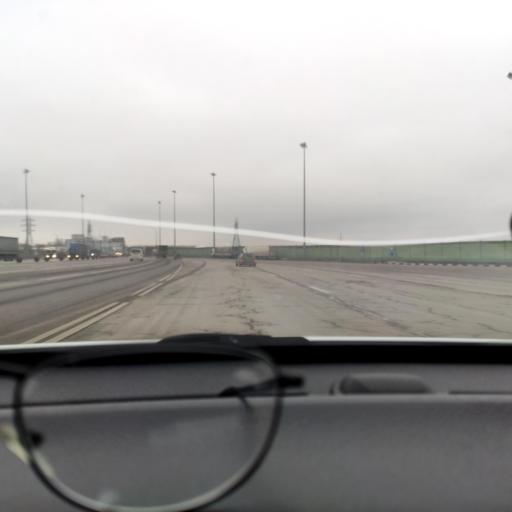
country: RU
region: Voronezj
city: Somovo
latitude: 51.6638
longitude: 39.3026
